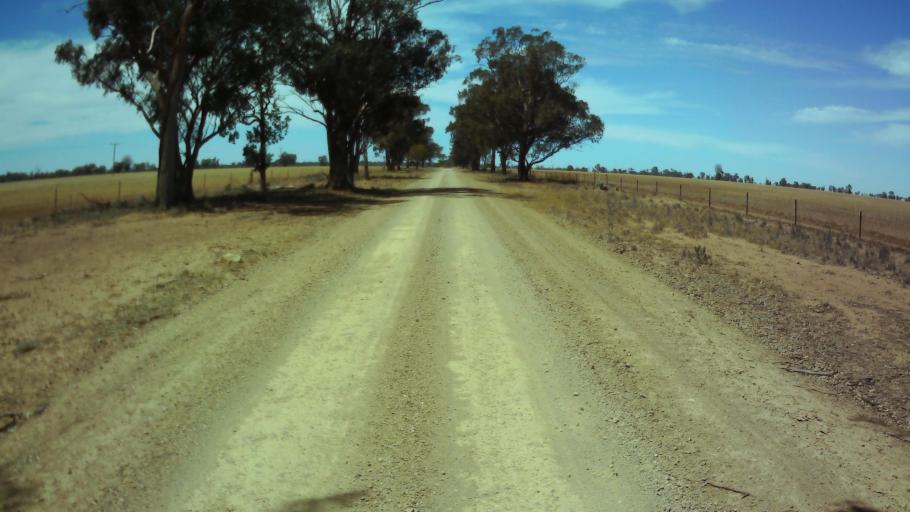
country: AU
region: New South Wales
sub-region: Weddin
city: Grenfell
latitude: -33.8710
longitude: 147.8063
